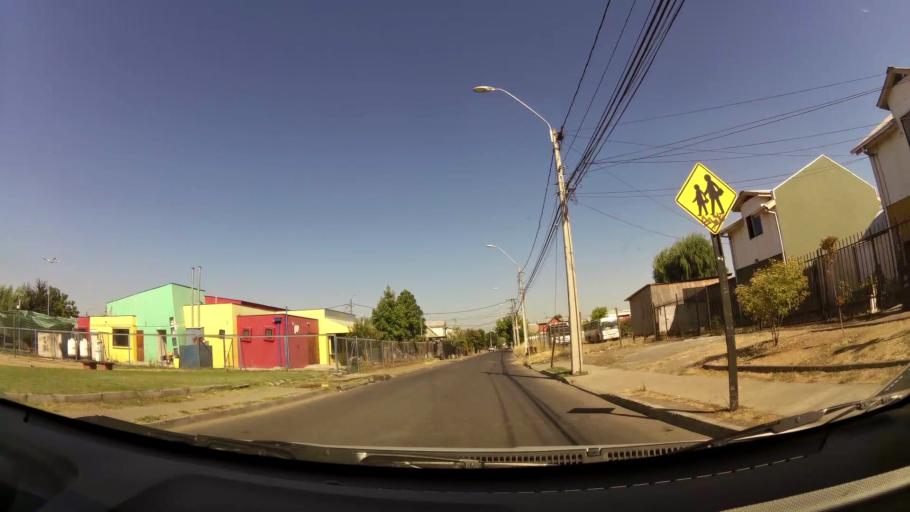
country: CL
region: Maule
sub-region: Provincia de Curico
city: Curico
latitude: -34.9812
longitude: -71.2575
